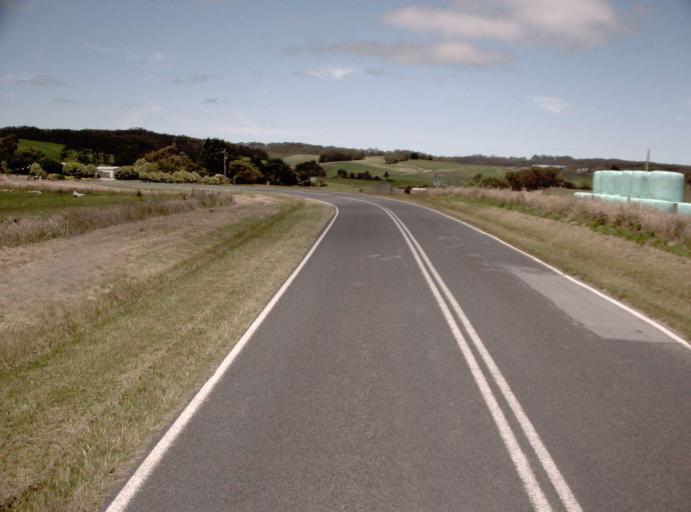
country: AU
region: Victoria
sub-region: Bass Coast
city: North Wonthaggi
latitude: -38.7138
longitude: 146.0993
